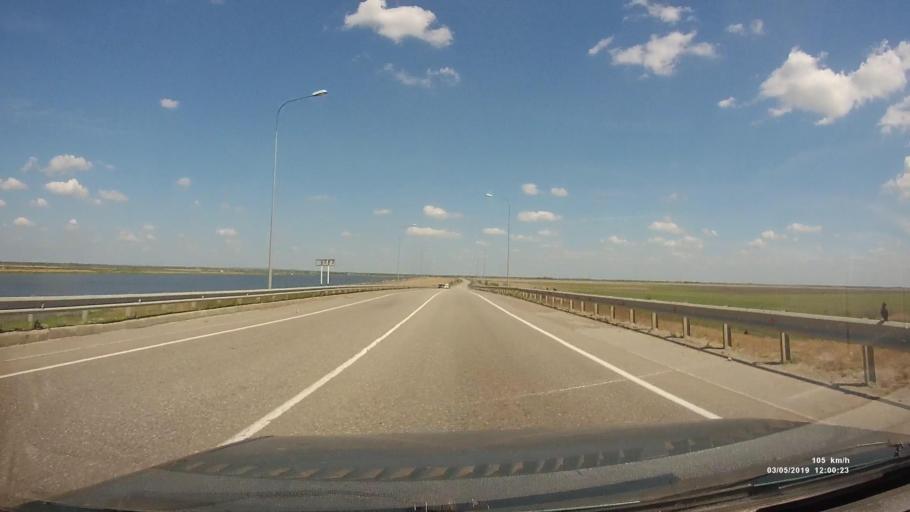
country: RU
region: Rostov
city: Bagayevskaya
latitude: 47.2492
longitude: 40.3407
